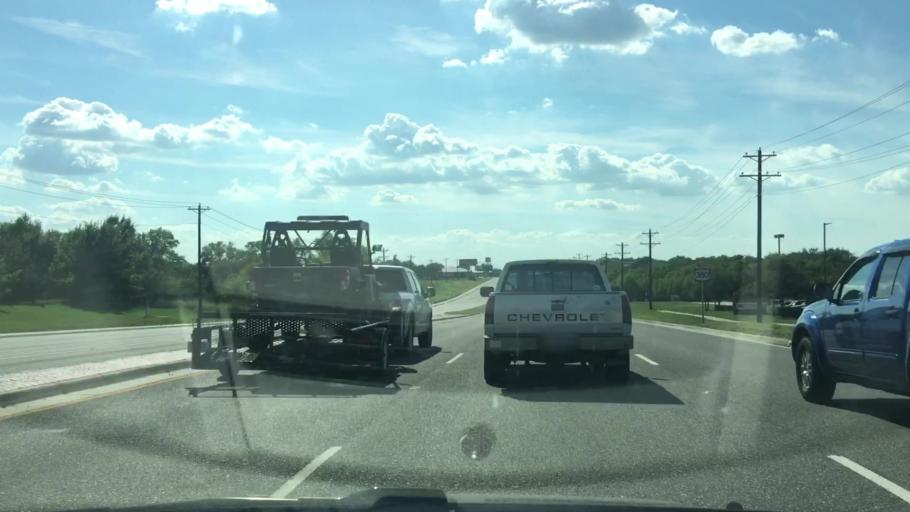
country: US
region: Texas
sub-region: Collin County
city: Prosper
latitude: 33.2185
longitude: -96.7354
